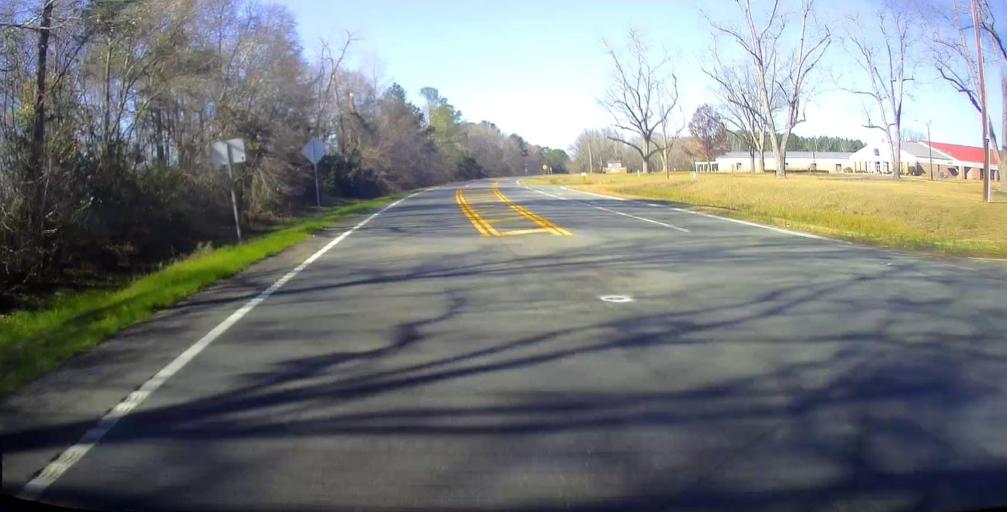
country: US
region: Georgia
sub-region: Macon County
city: Oglethorpe
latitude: 32.2869
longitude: -84.0747
